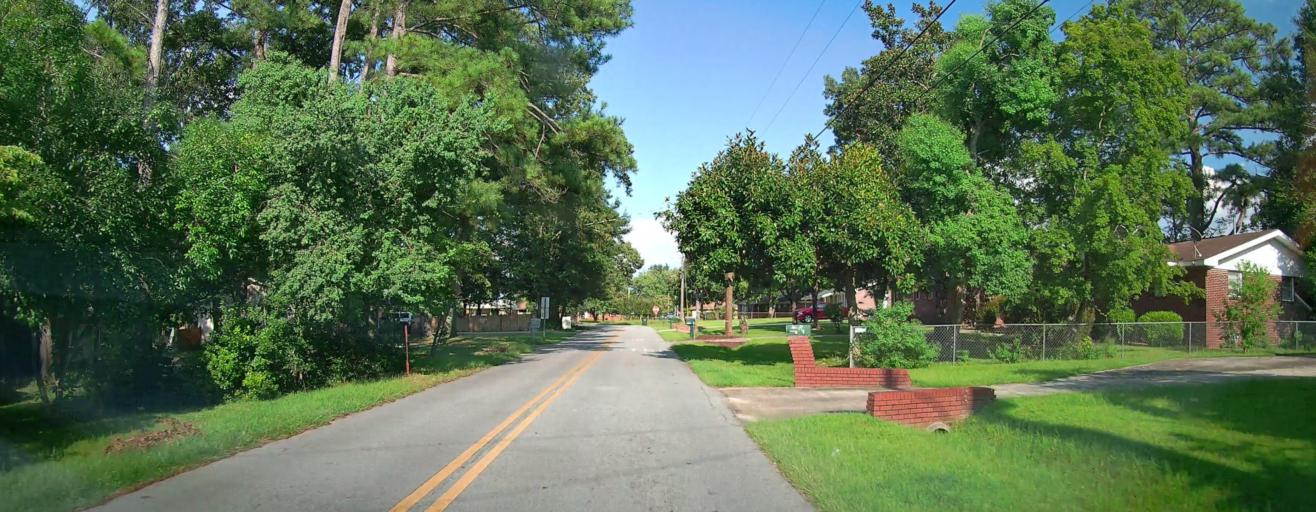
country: US
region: Georgia
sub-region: Houston County
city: Warner Robins
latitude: 32.5994
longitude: -83.6432
